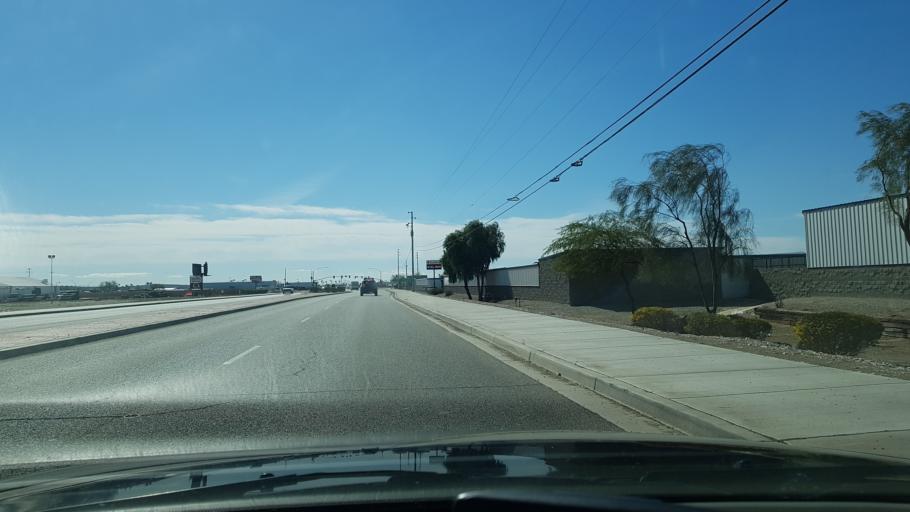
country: US
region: Arizona
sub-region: Yuma County
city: Yuma
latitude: 32.6730
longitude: -114.5817
